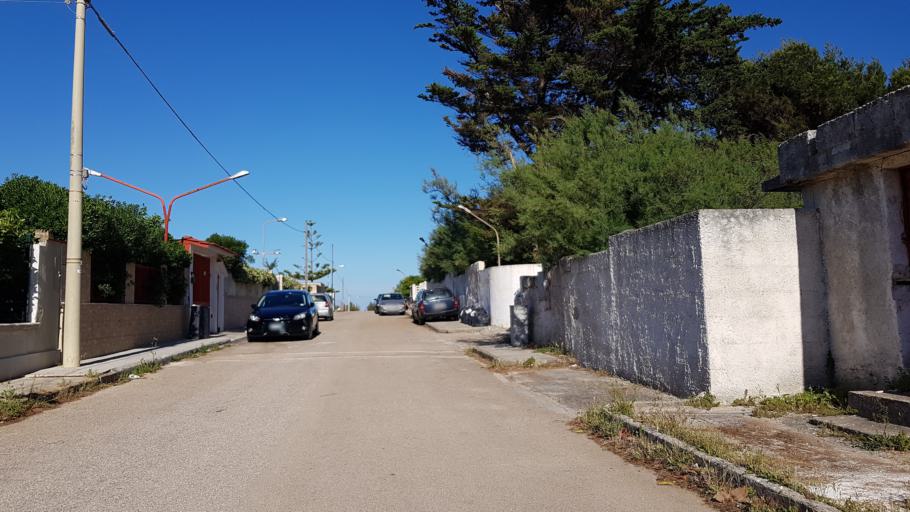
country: IT
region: Apulia
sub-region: Provincia di Brindisi
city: Brindisi
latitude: 40.6840
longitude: 17.8730
